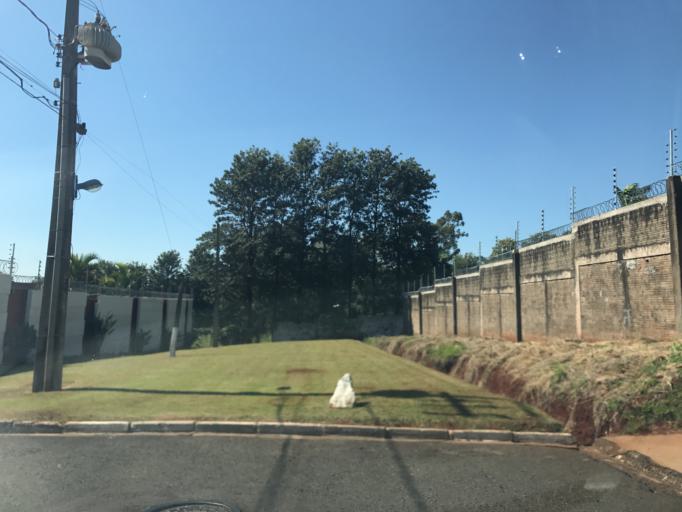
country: BR
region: Parana
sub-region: Maringa
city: Maringa
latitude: -23.4415
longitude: -51.9517
